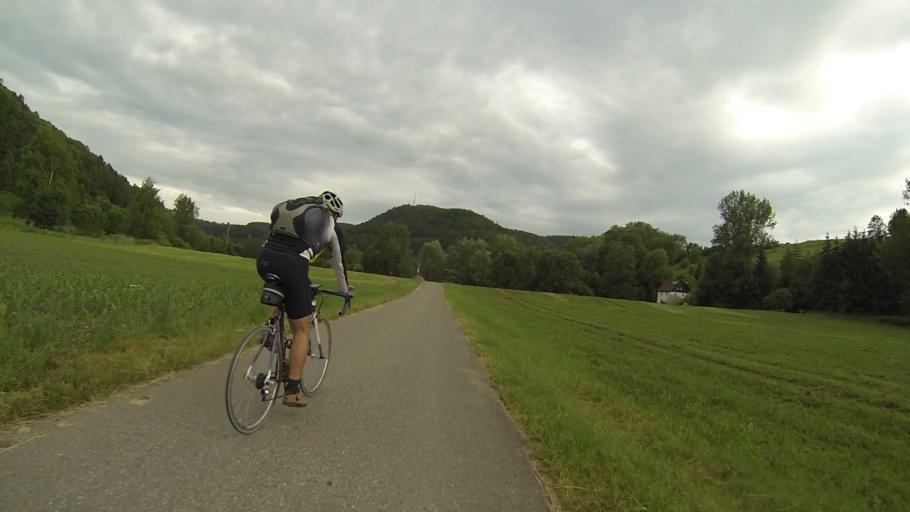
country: DE
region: Baden-Wuerttemberg
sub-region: Tuebingen Region
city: Blaubeuren
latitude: 48.4072
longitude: 9.7974
